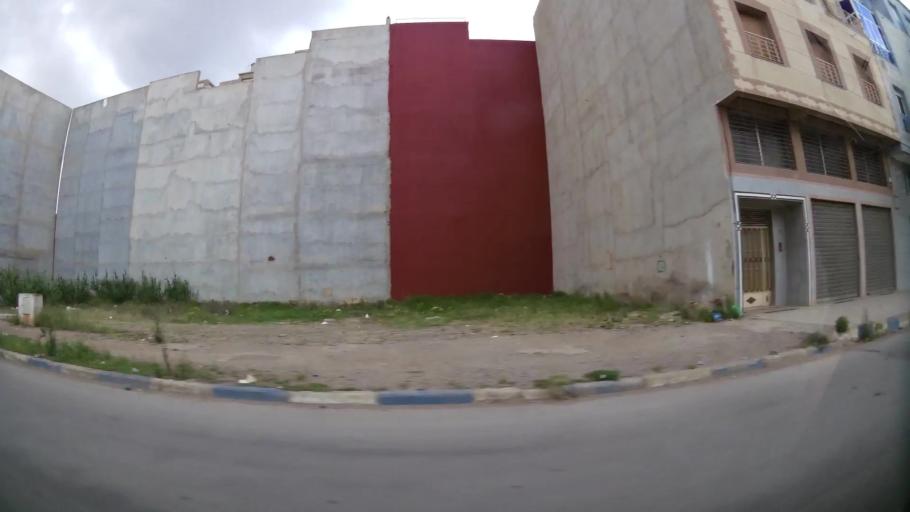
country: MA
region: Oriental
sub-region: Nador
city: Nador
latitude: 35.1551
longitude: -2.9282
